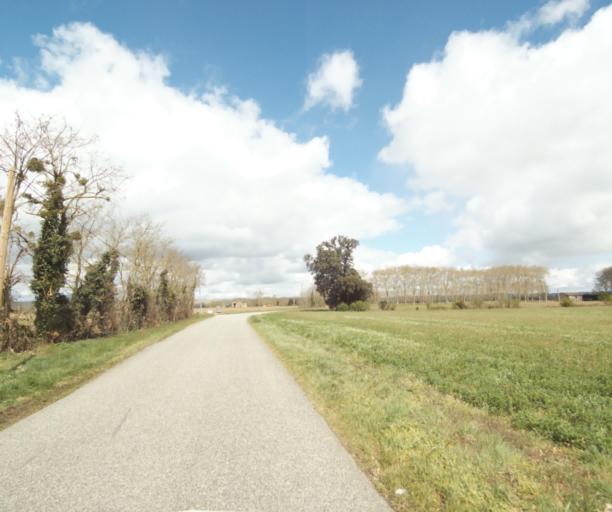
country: FR
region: Midi-Pyrenees
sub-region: Departement de l'Ariege
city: Saverdun
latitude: 43.2549
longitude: 1.5995
